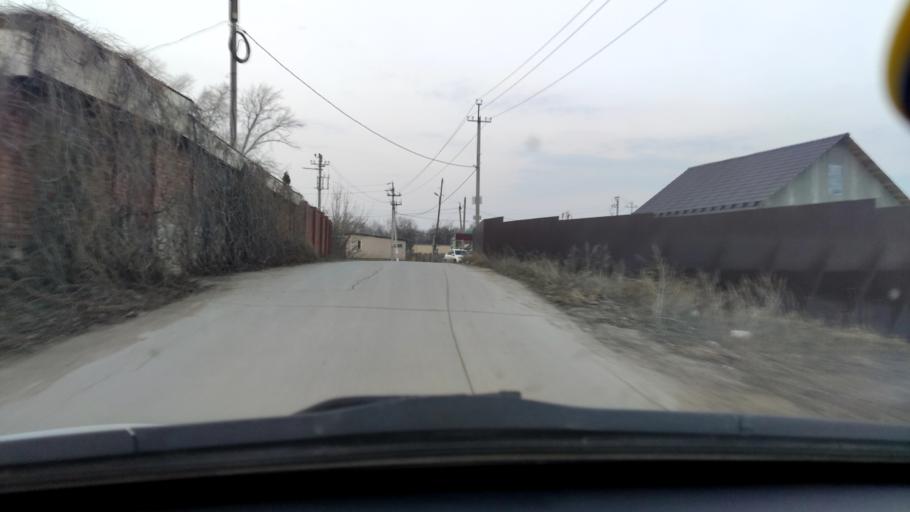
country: RU
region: Samara
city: Zhigulevsk
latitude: 53.4561
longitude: 49.5174
